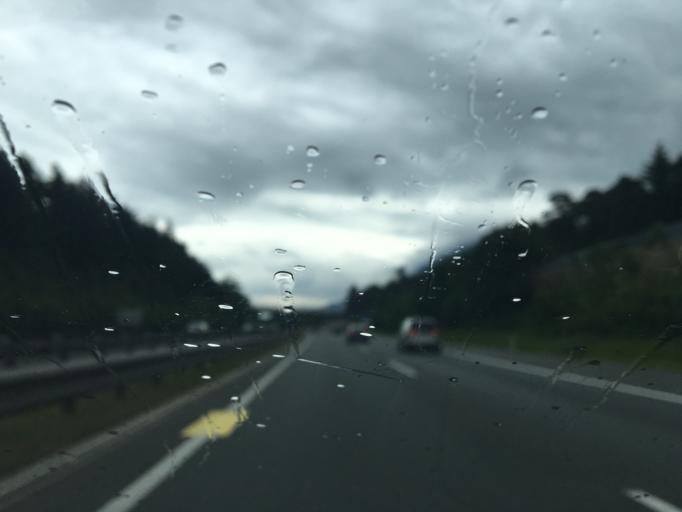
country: AT
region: Tyrol
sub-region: Politischer Bezirk Schwaz
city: Pill
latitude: 47.3238
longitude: 11.6689
